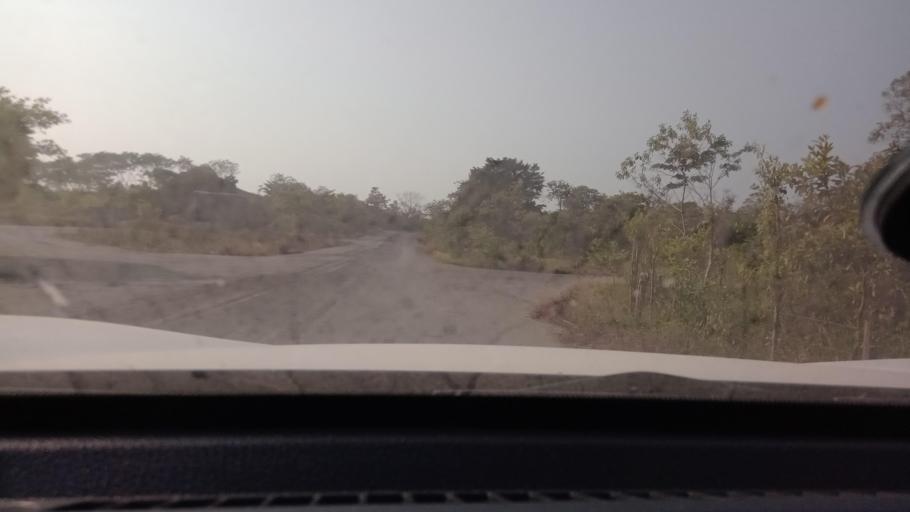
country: MX
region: Tabasco
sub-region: Huimanguillo
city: Francisco Rueda
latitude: 17.6654
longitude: -93.8666
